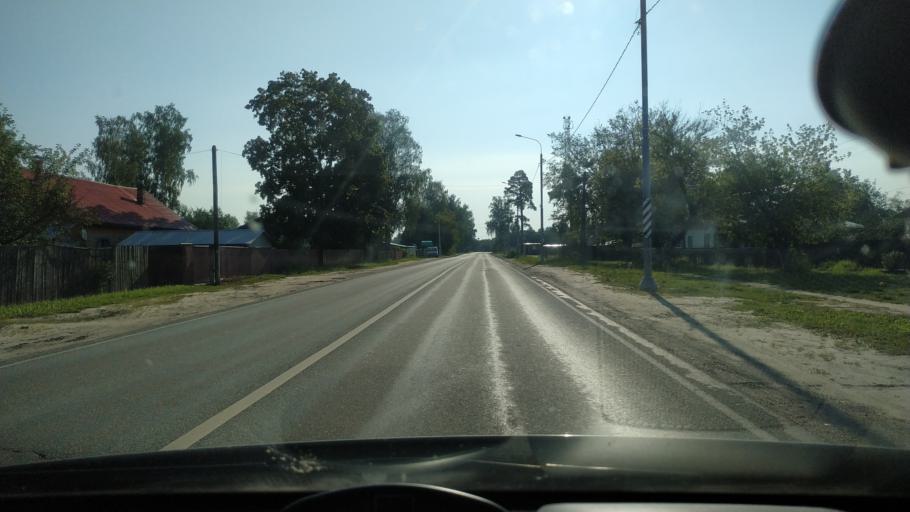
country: RU
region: Moskovskaya
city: Kerva
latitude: 55.5621
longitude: 39.6694
